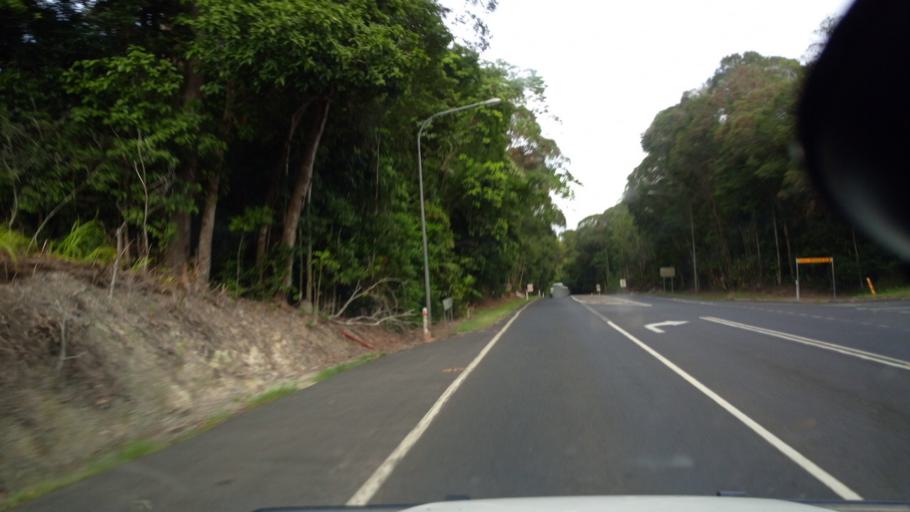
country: AU
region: Queensland
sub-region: Tablelands
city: Kuranda
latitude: -16.8154
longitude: 145.6412
